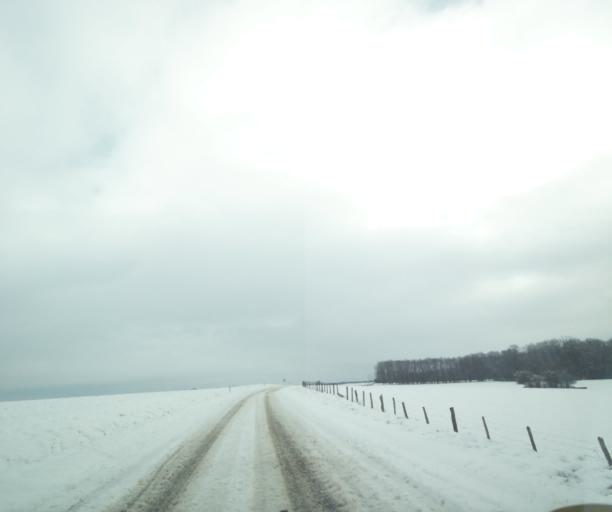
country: FR
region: Champagne-Ardenne
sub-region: Departement de la Haute-Marne
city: Montier-en-Der
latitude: 48.5194
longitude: 4.6776
